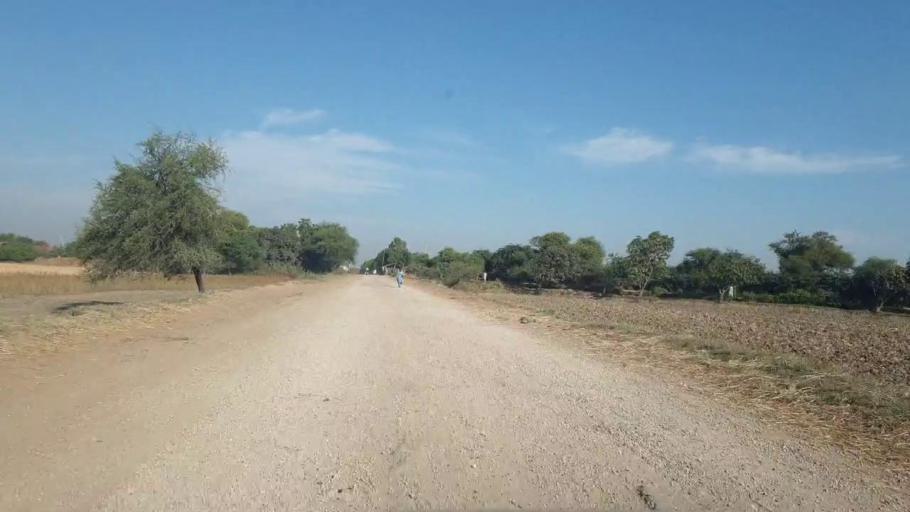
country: PK
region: Sindh
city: Talhar
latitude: 24.9440
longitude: 68.7874
